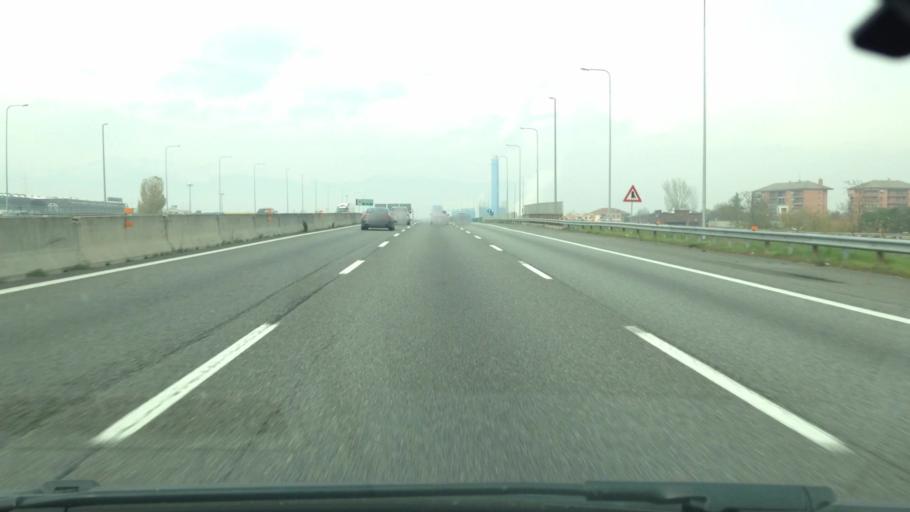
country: IT
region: Piedmont
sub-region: Provincia di Torino
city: Fornaci
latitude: 45.0243
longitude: 7.5963
